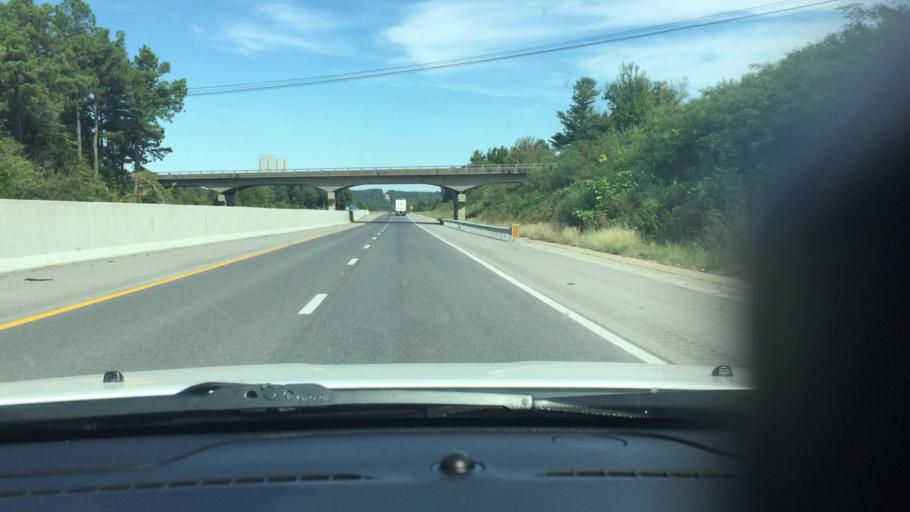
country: US
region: Kentucky
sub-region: Caldwell County
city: Princeton
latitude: 37.1323
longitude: -87.8723
